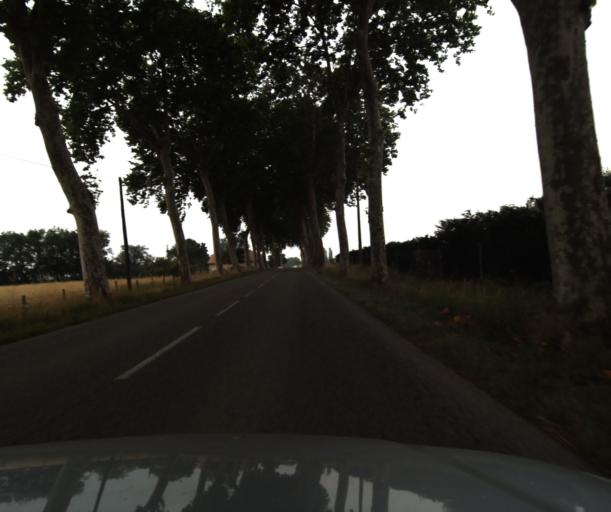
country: FR
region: Midi-Pyrenees
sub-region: Departement du Tarn-et-Garonne
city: Beaumont-de-Lomagne
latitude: 43.8481
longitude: 0.9380
